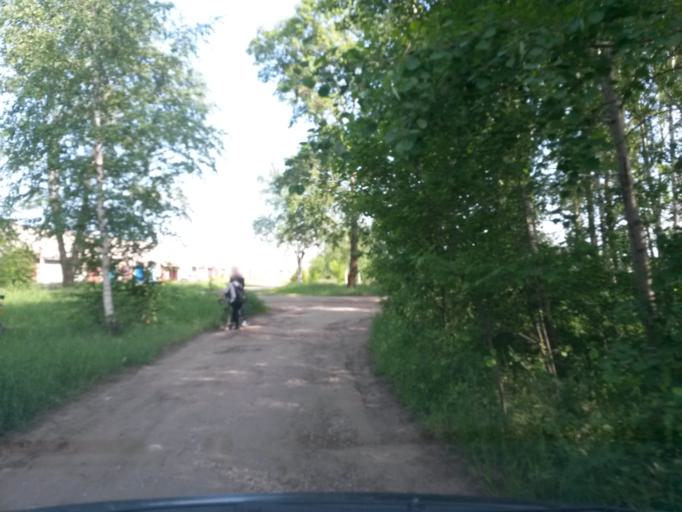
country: RU
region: Jaroslavl
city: Yaroslavl
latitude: 57.6407
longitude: 39.7887
